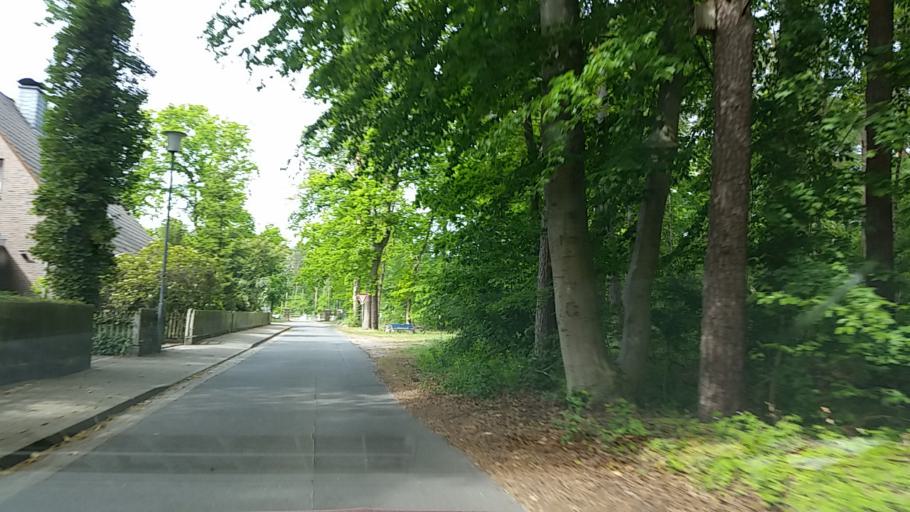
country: DE
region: Lower Saxony
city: Bodenteich
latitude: 52.8417
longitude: 10.6734
